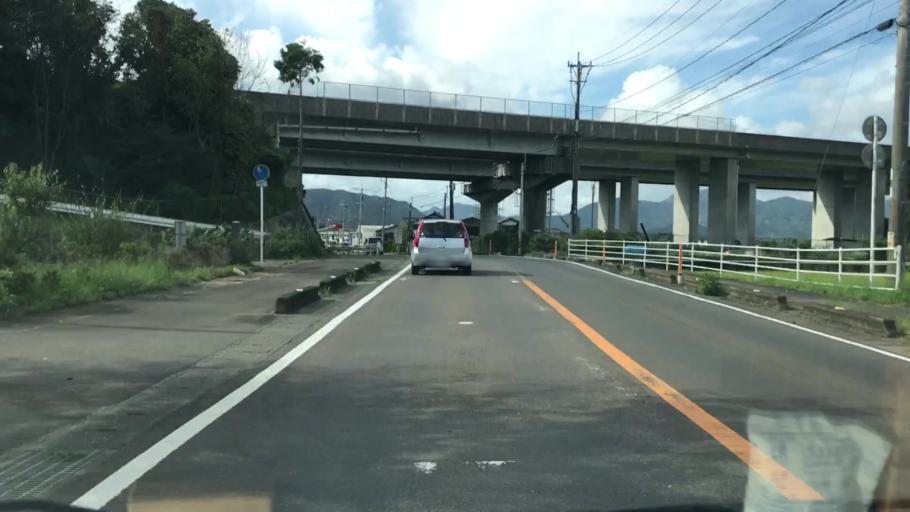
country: JP
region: Saga Prefecture
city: Takeocho-takeo
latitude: 33.1767
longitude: 130.0467
